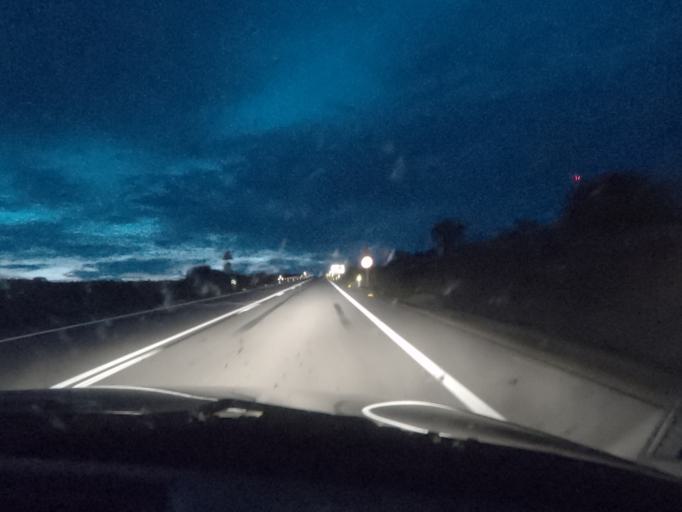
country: ES
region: Extremadura
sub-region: Provincia de Caceres
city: Carcaboso
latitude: 39.9807
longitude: -6.1646
